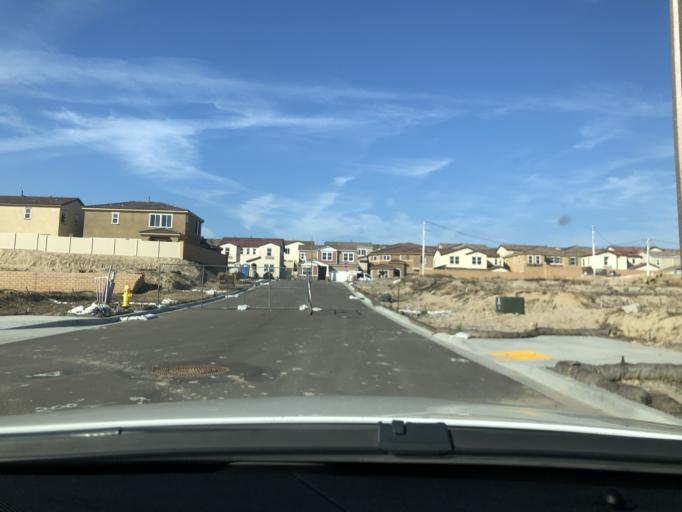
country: US
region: California
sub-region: San Diego County
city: Bonita
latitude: 32.6059
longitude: -116.9953
